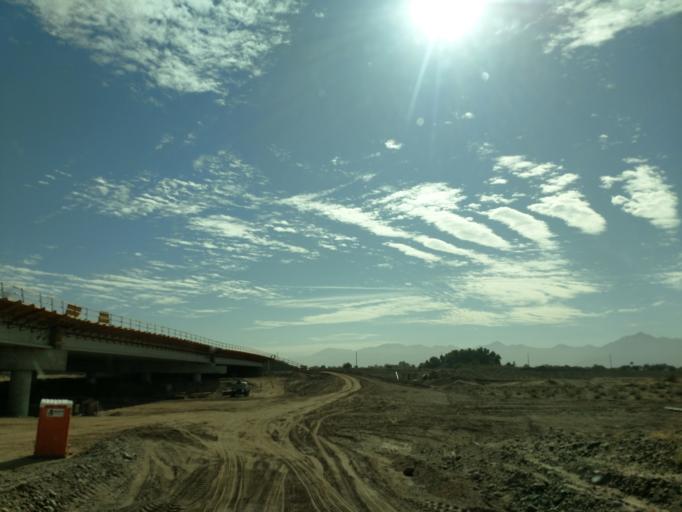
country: US
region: Arizona
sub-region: Maricopa County
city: Laveen
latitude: 33.3968
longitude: -112.1928
